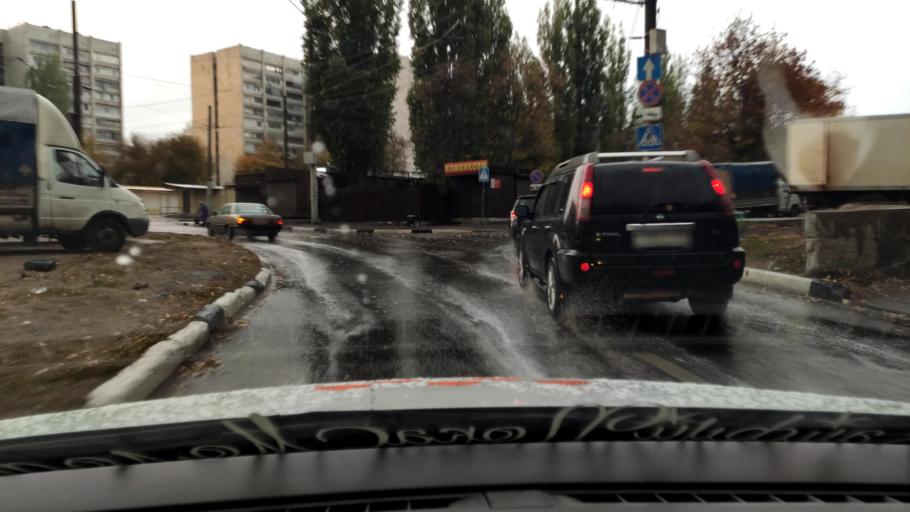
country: RU
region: Voronezj
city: Podgornoye
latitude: 51.7022
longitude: 39.1638
